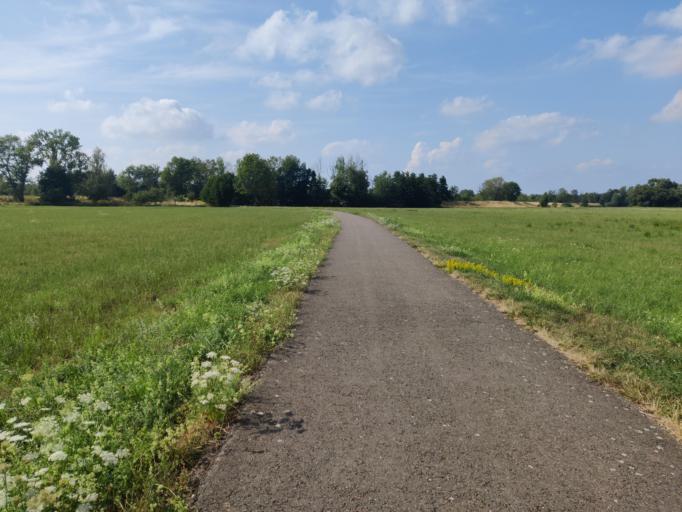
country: DE
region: Thuringia
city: Haselbach
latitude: 51.0649
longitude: 12.4450
